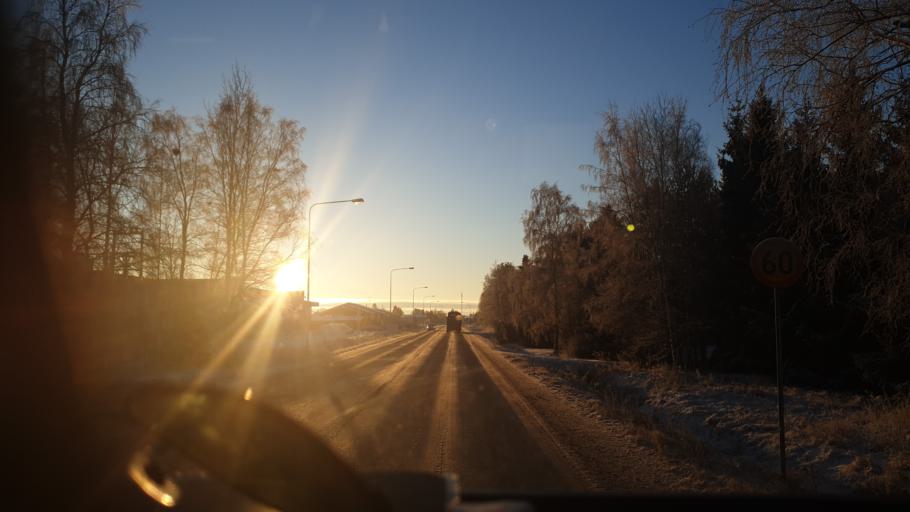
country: FI
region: Northern Ostrobothnia
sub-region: Ylivieska
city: Kalajoki
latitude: 64.2688
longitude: 23.9491
